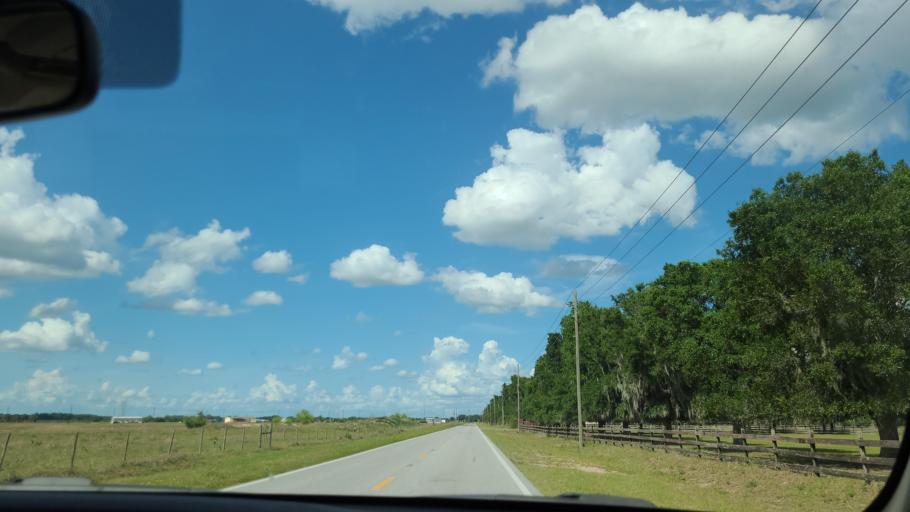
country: US
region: Florida
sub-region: Polk County
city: Lake Wales
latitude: 27.9198
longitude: -81.5446
